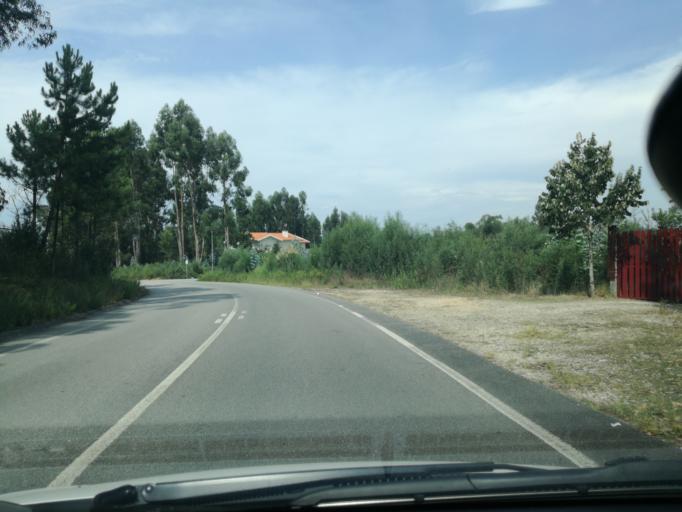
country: PT
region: Aveiro
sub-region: Santa Maria da Feira
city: Nogueira da Regedoura
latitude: 41.0138
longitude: -8.5858
